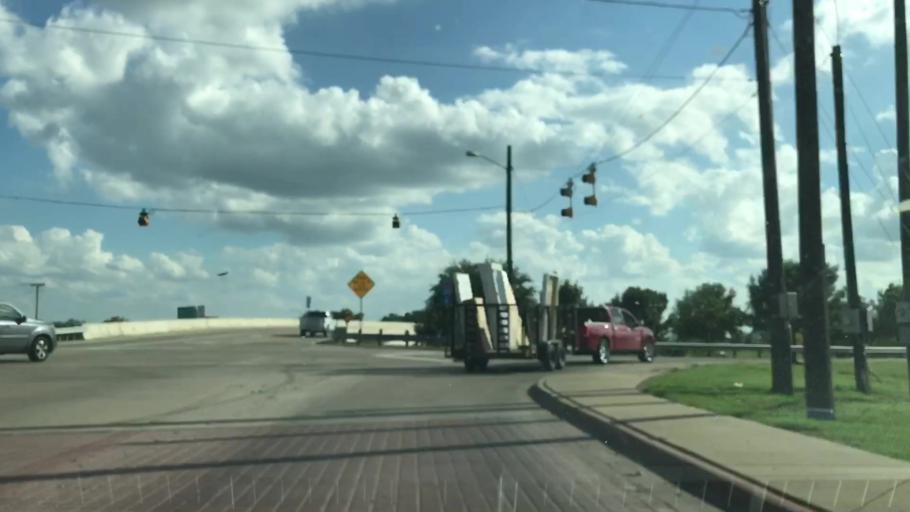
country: US
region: Texas
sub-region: Dallas County
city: Rowlett
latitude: 32.8773
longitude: -96.5184
